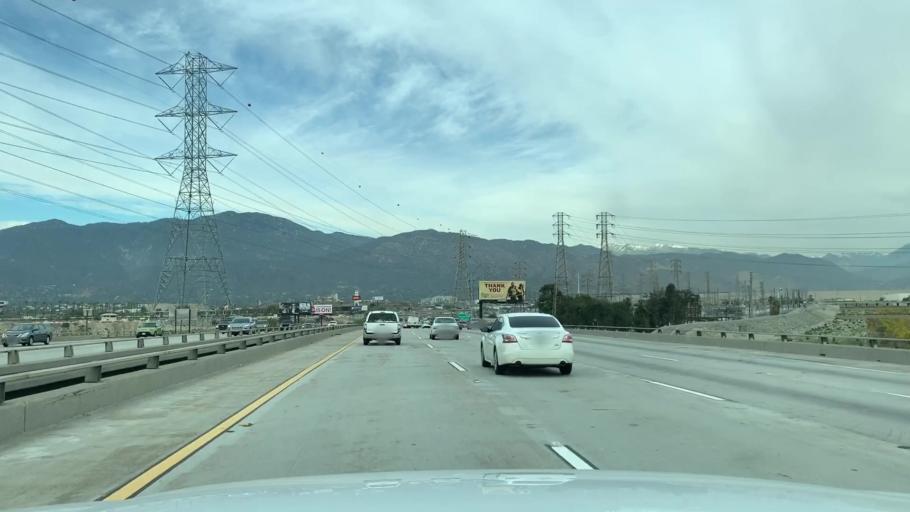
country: US
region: California
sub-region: Los Angeles County
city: Baldwin Park
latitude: 34.1001
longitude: -117.9848
